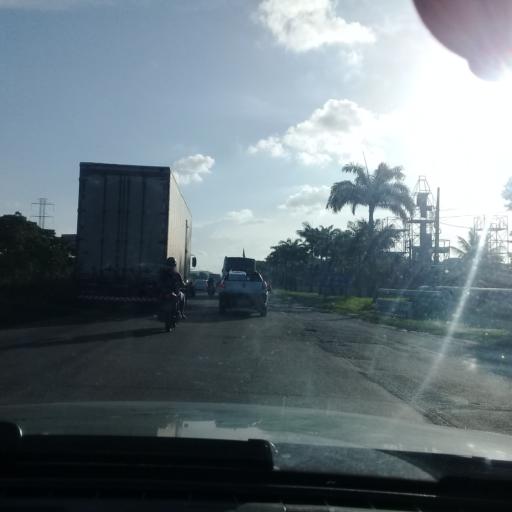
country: BR
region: Pernambuco
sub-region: Recife
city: Recife
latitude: -8.0694
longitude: -34.9491
